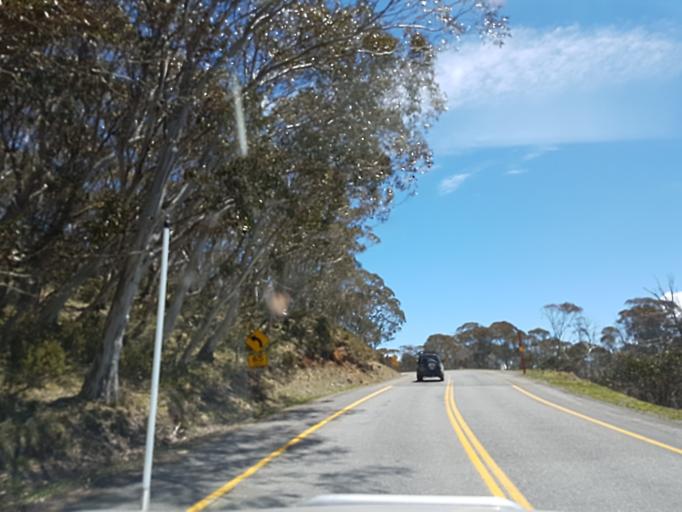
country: AU
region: Victoria
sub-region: Alpine
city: Mount Beauty
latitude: -37.0207
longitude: 147.2625
